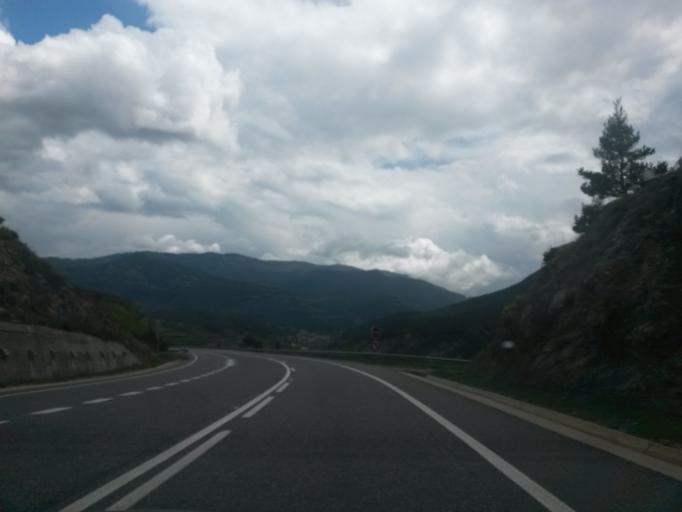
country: ES
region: Catalonia
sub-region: Provincia de Barcelona
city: Baga
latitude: 42.2601
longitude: 1.8557
